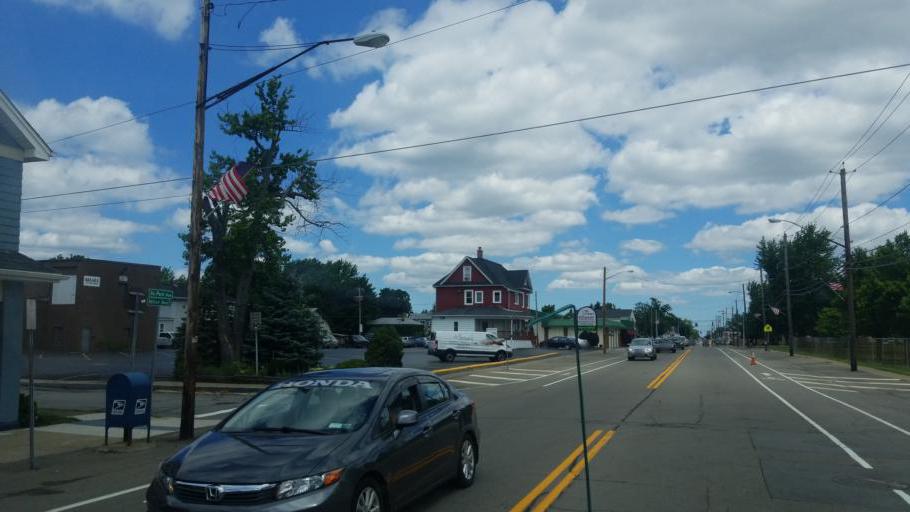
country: US
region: New York
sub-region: Erie County
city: Blasdell
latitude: 42.7940
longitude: -78.8239
